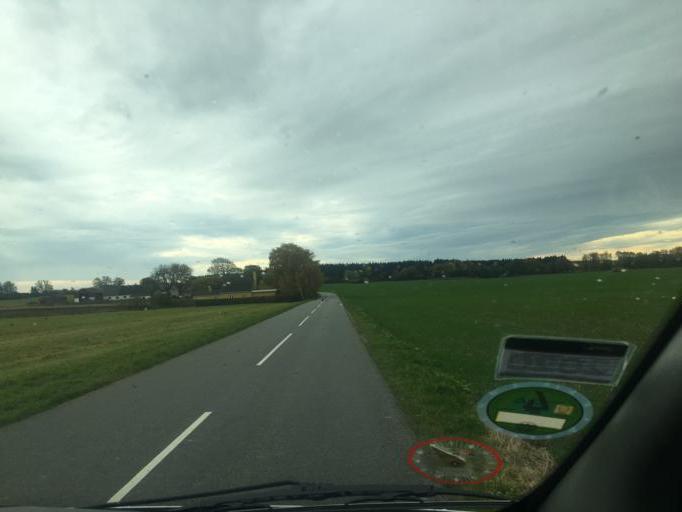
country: DK
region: Zealand
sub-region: Koge Kommune
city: Bjaeverskov
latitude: 55.4238
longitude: 11.9817
